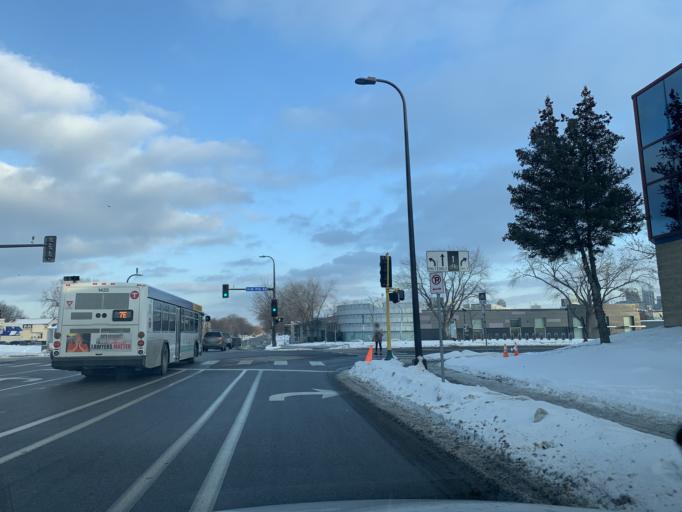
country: US
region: Minnesota
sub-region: Hennepin County
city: Minneapolis
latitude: 44.9919
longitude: -93.2946
